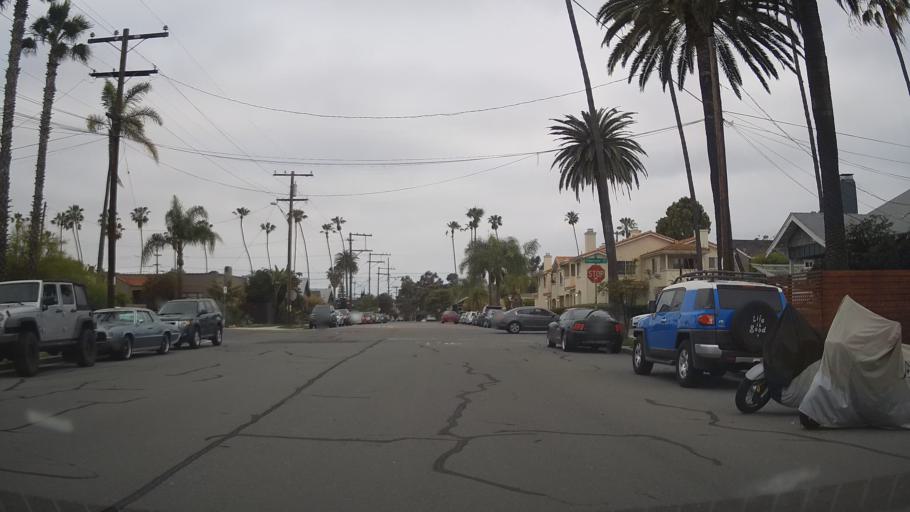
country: US
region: California
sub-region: San Diego County
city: San Diego
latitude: 32.7591
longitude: -117.1496
